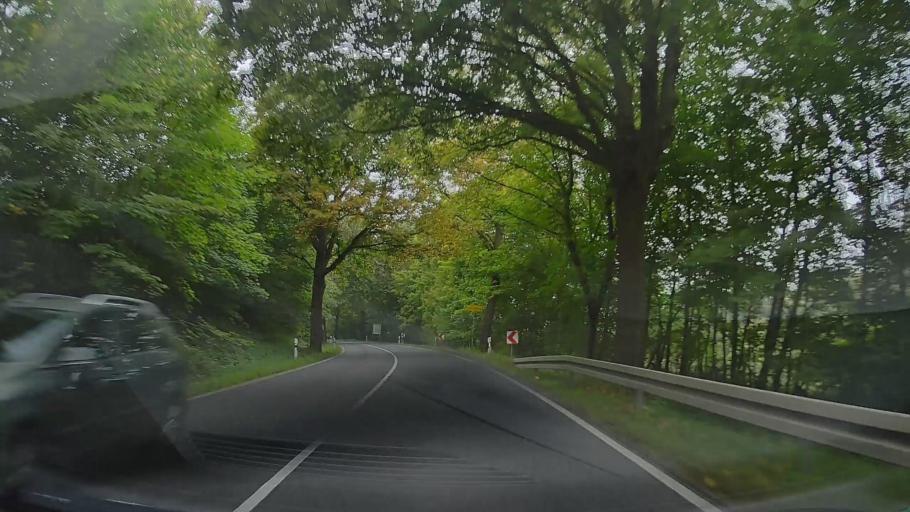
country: DE
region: Mecklenburg-Vorpommern
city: Sternberg
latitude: 53.7059
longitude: 11.8395
